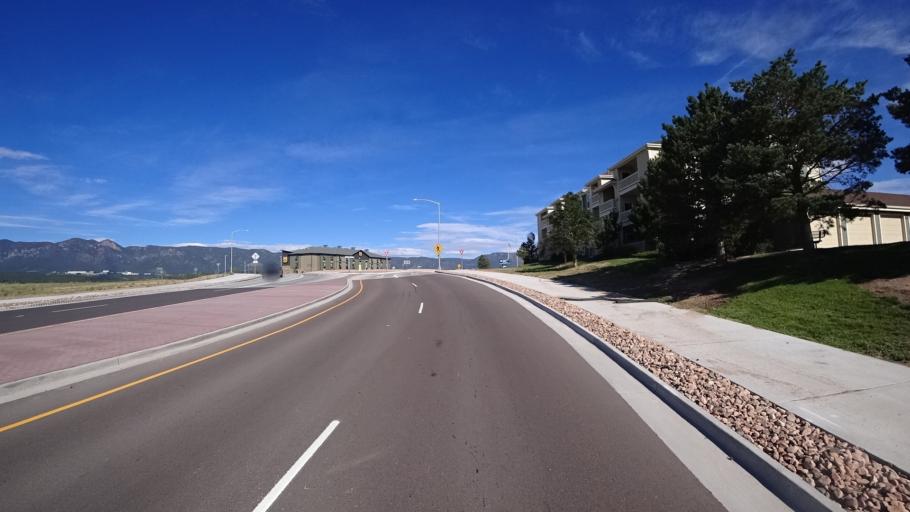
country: US
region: Colorado
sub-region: El Paso County
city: Gleneagle
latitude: 39.0304
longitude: -104.8299
